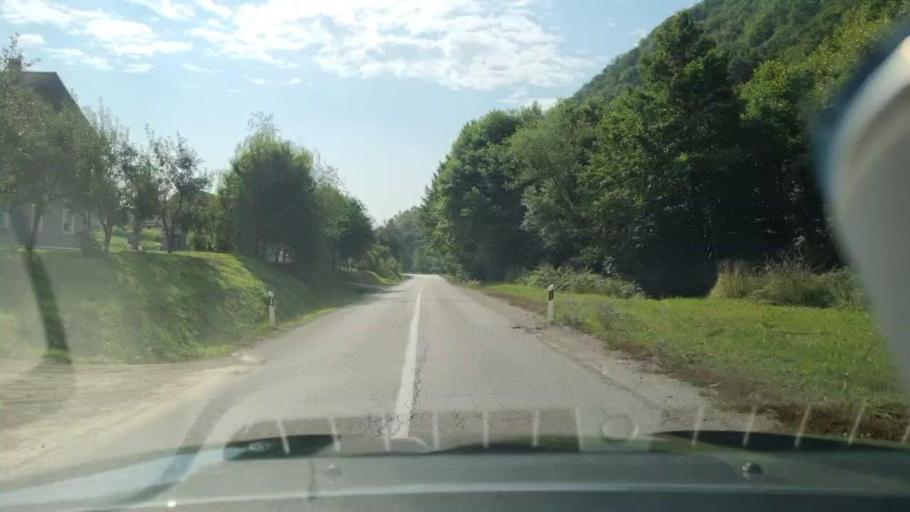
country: BA
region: Federation of Bosnia and Herzegovina
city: Jezerski
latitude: 45.0048
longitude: 16.1320
